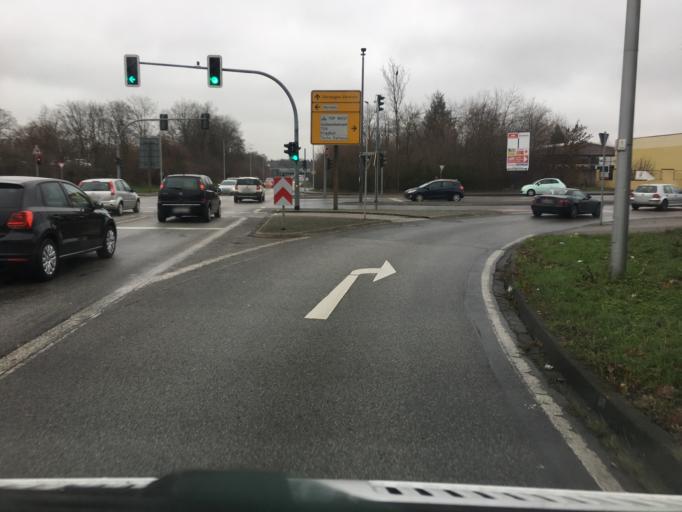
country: DE
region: North Rhine-Westphalia
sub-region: Regierungsbezirk Dusseldorf
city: Dormagen
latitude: 51.0957
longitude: 6.8125
